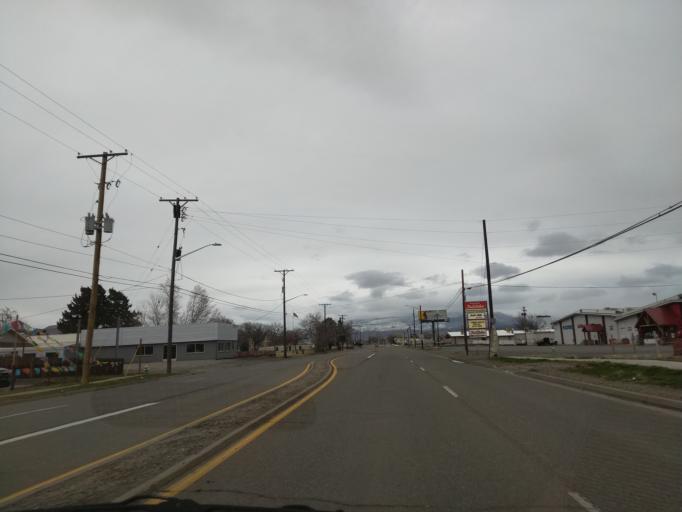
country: US
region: Colorado
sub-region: Mesa County
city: Fruitvale
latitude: 39.0773
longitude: -108.5044
